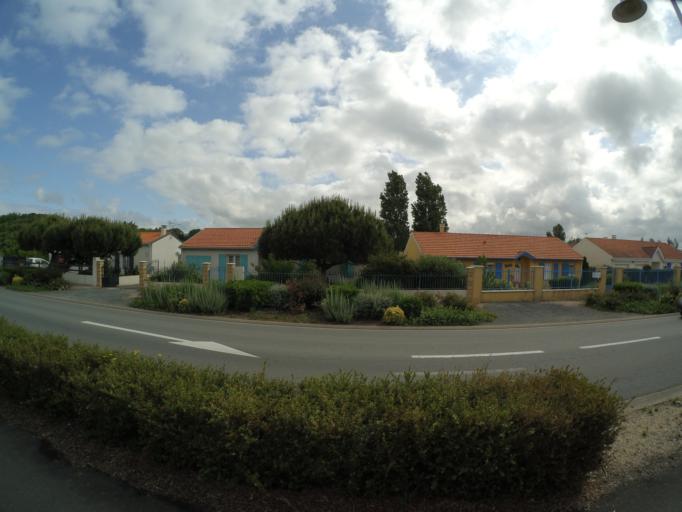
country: FR
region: Poitou-Charentes
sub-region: Departement de la Charente-Maritime
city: Chatelaillon-Plage
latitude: 46.0870
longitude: -1.0956
